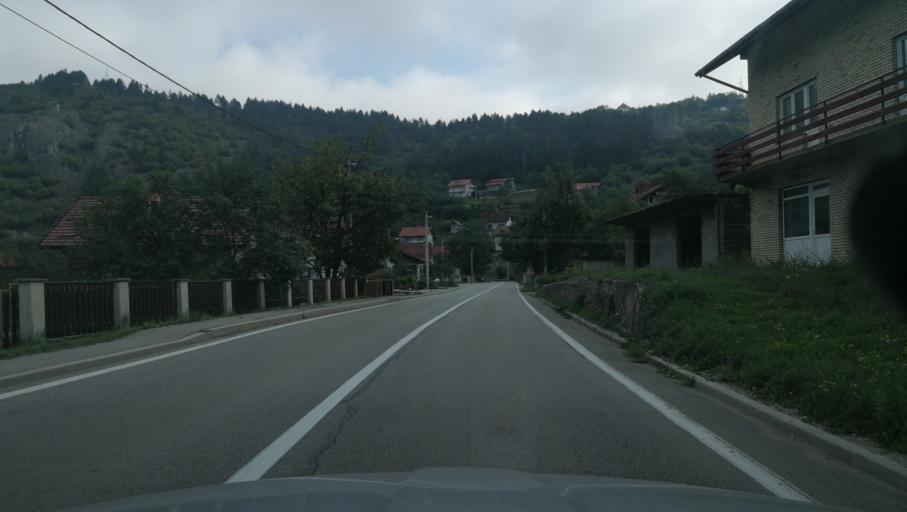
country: BA
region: Federation of Bosnia and Herzegovina
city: Divicani
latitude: 44.3677
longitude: 17.2991
